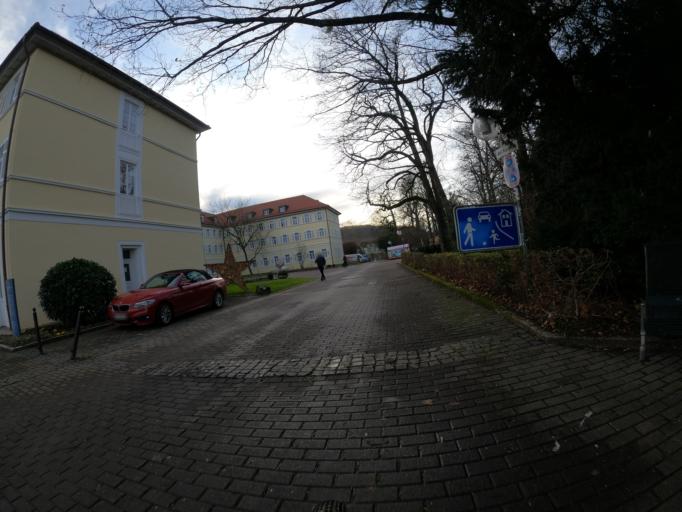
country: DE
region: Baden-Wuerttemberg
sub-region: Regierungsbezirk Stuttgart
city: Boll
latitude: 48.6399
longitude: 9.6001
